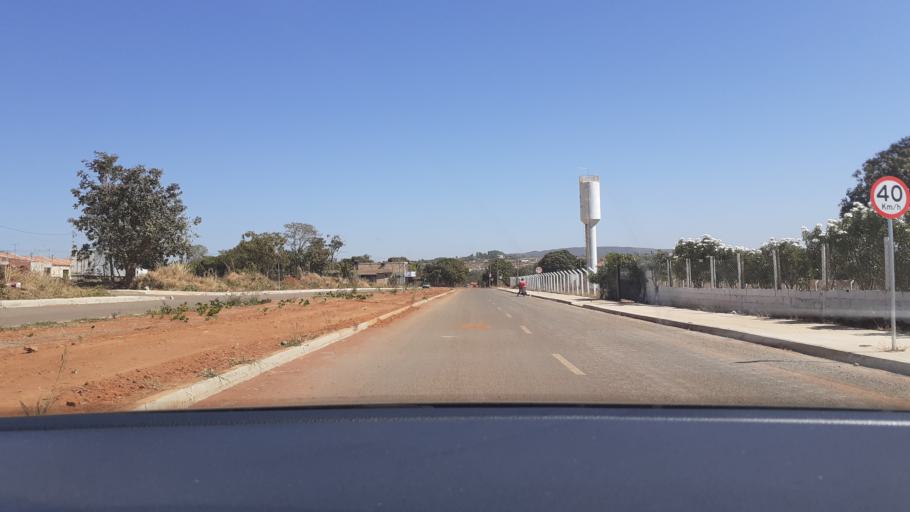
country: BR
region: Goias
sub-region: Aparecida De Goiania
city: Aparecida de Goiania
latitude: -16.8795
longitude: -49.2552
